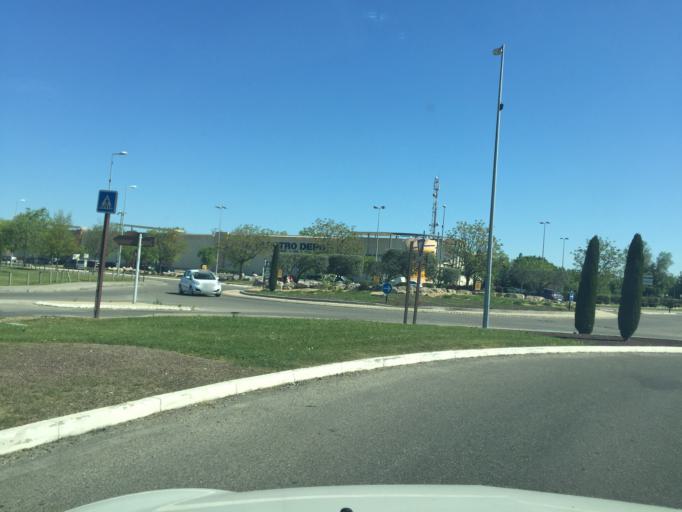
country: FR
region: Provence-Alpes-Cote d'Azur
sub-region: Departement du Vaucluse
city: Montfavet
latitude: 43.9215
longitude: 4.8675
